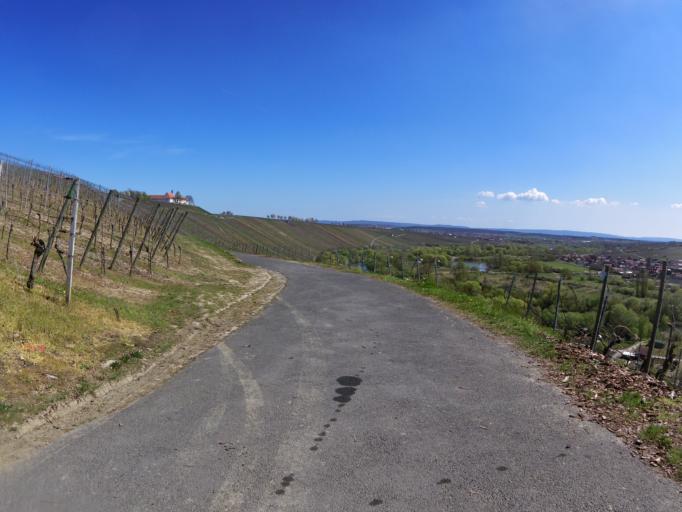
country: DE
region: Bavaria
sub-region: Regierungsbezirk Unterfranken
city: Nordheim
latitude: 49.8639
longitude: 10.1745
